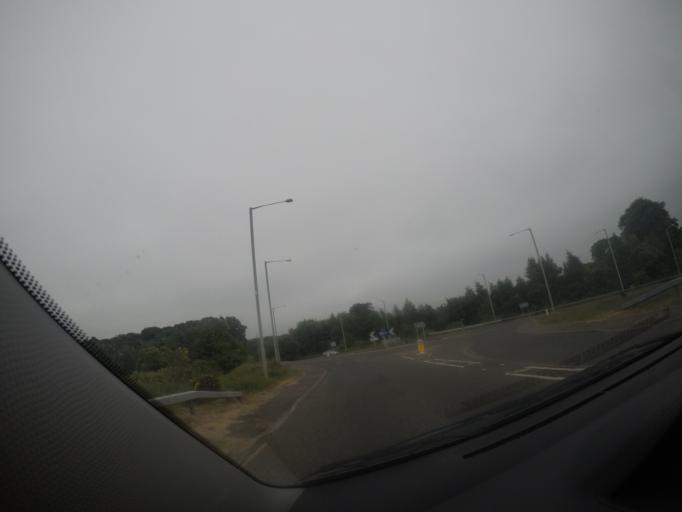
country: GB
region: Scotland
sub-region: Angus
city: Brechin
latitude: 56.7288
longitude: -2.6982
